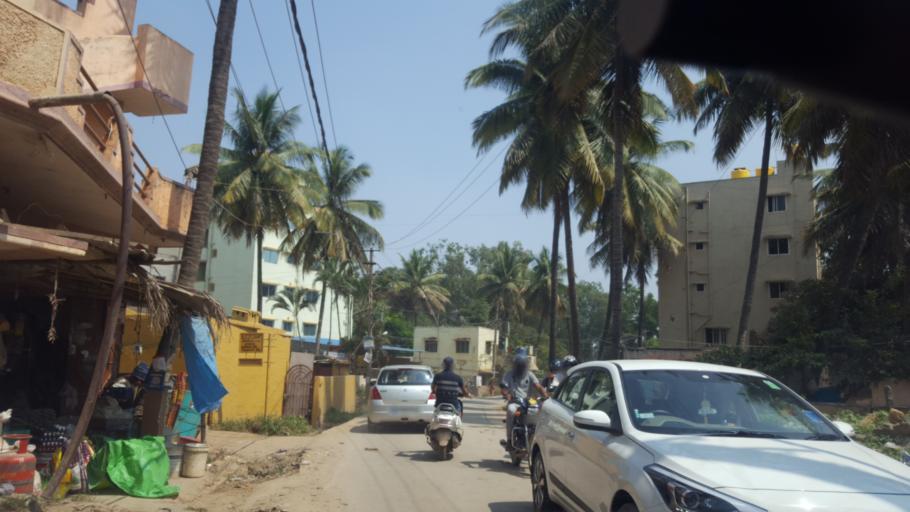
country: IN
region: Karnataka
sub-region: Bangalore Urban
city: Bangalore
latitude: 12.9356
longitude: 77.7061
